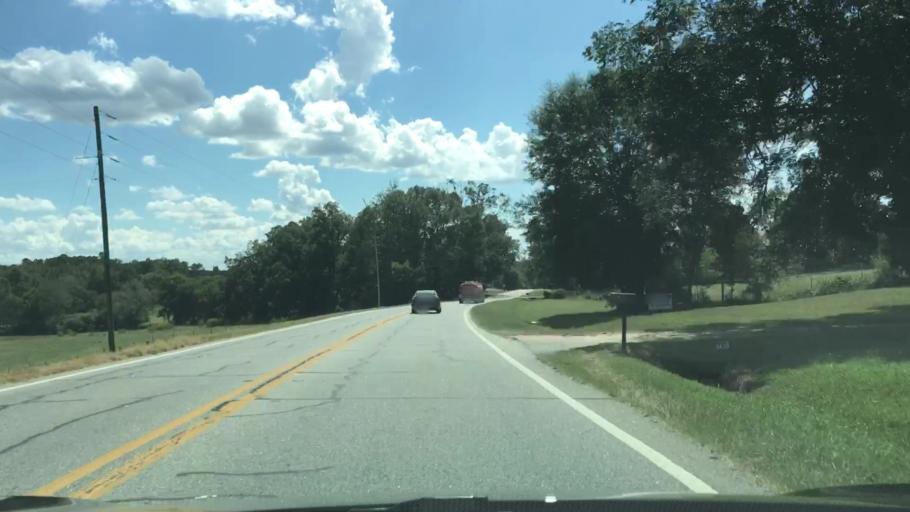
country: US
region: Georgia
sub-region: Oconee County
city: Watkinsville
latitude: 33.7474
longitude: -83.3012
